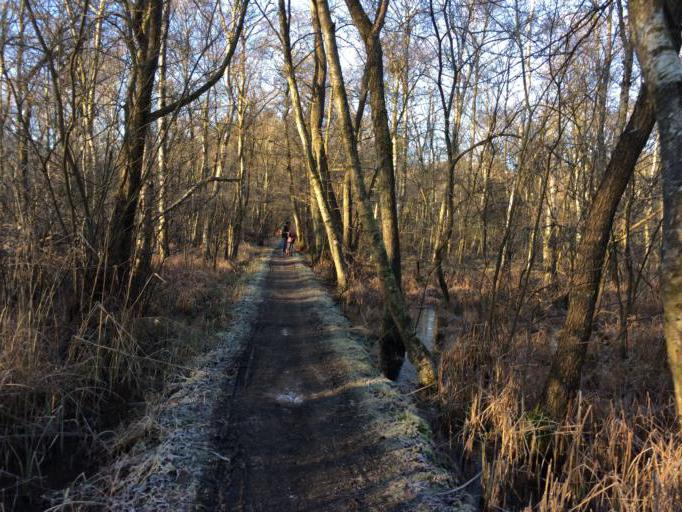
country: DK
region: Capital Region
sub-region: Gladsaxe Municipality
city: Buddinge
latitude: 55.7788
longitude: 12.4630
